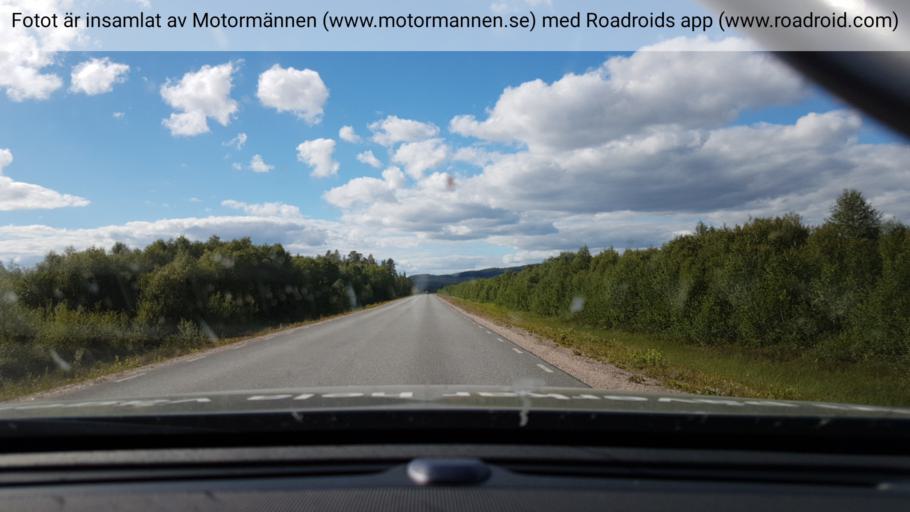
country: SE
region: Norrbotten
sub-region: Arjeplogs Kommun
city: Arjeplog
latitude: 66.0759
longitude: 17.5616
